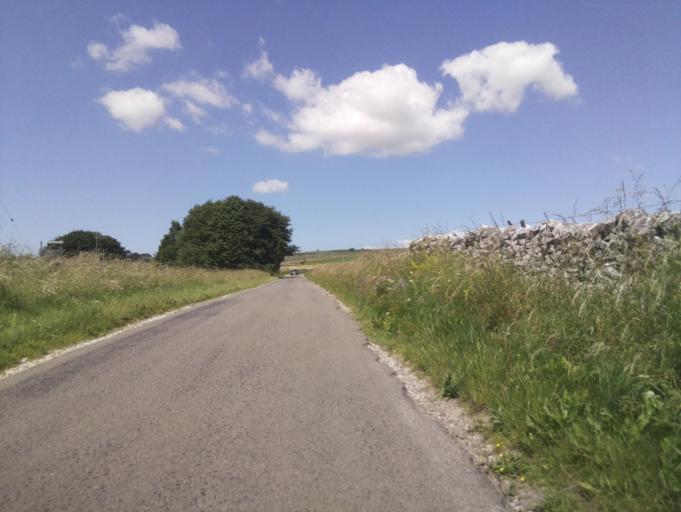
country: GB
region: England
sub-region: Derbyshire
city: Tideswell
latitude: 53.2147
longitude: -1.7809
